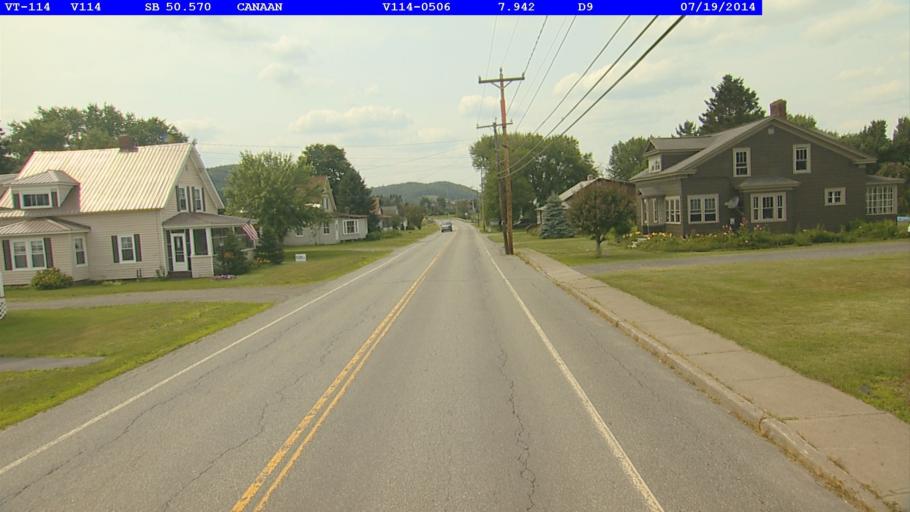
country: US
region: New Hampshire
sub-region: Coos County
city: Colebrook
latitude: 44.9984
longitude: -71.5421
